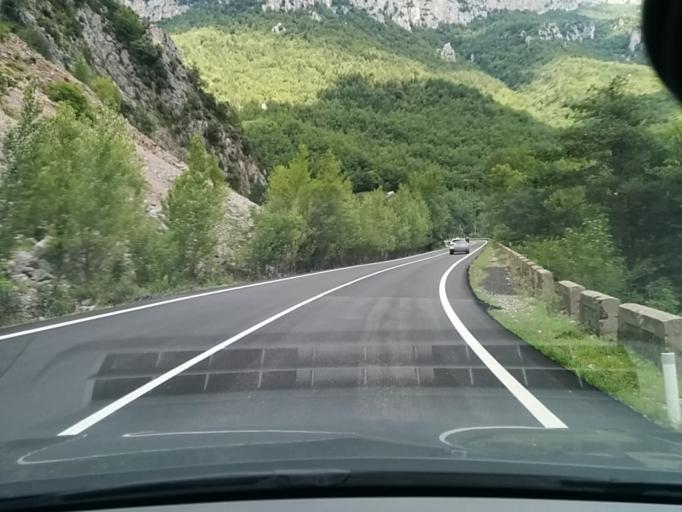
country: ES
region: Aragon
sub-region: Provincia de Huesca
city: Bielsa
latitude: 42.5796
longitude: 0.2021
